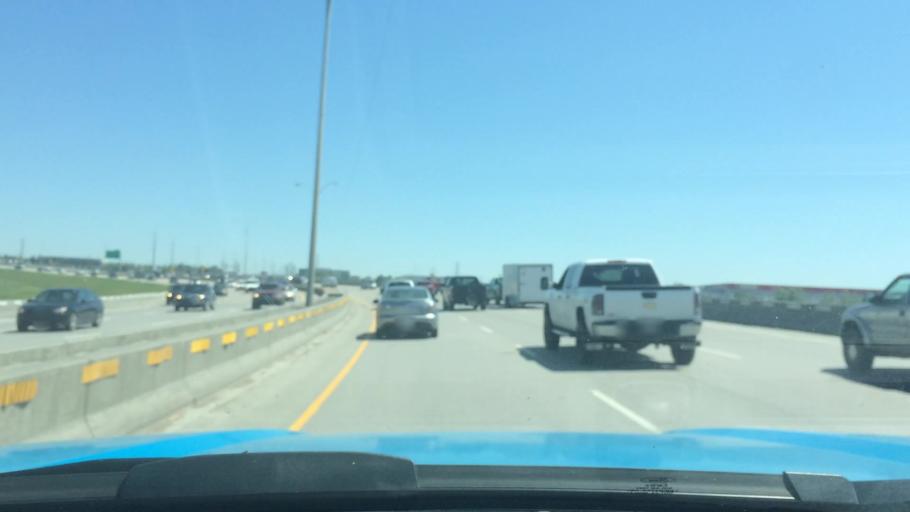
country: CA
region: Alberta
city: Calgary
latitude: 51.0084
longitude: -114.0184
